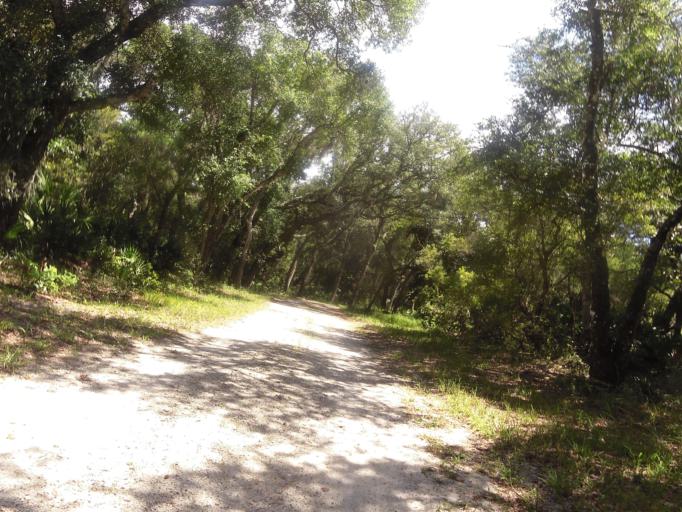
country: US
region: Florida
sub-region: Saint Johns County
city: Villano Beach
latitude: 30.0355
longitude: -81.3360
